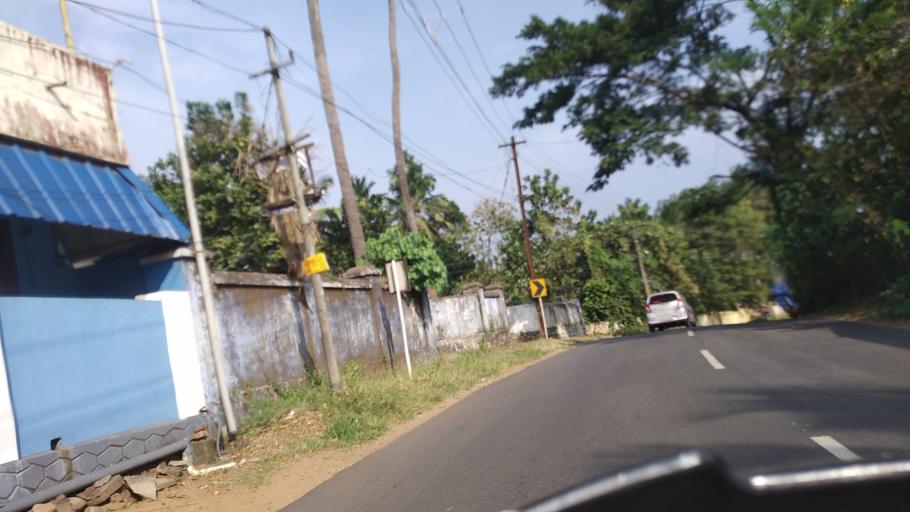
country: IN
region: Kerala
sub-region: Palakkad district
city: Palakkad
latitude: 10.6017
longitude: 76.5467
